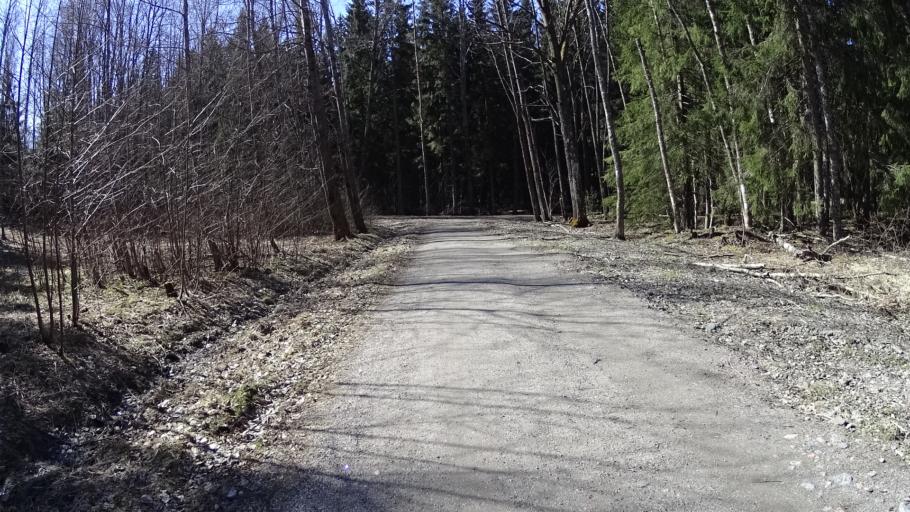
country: FI
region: Uusimaa
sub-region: Helsinki
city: Espoo
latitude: 60.2344
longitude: 24.6421
